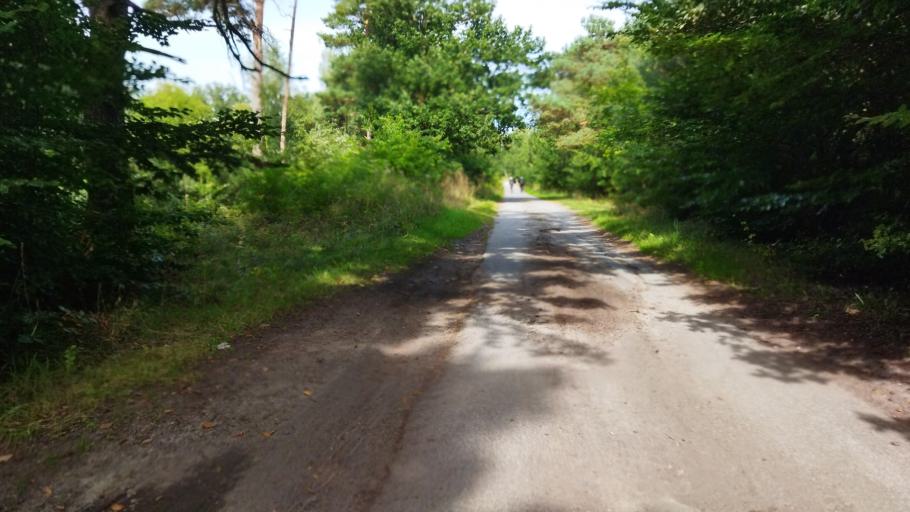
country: DE
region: Lower Saxony
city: Glandorf
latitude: 52.0957
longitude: 8.0359
